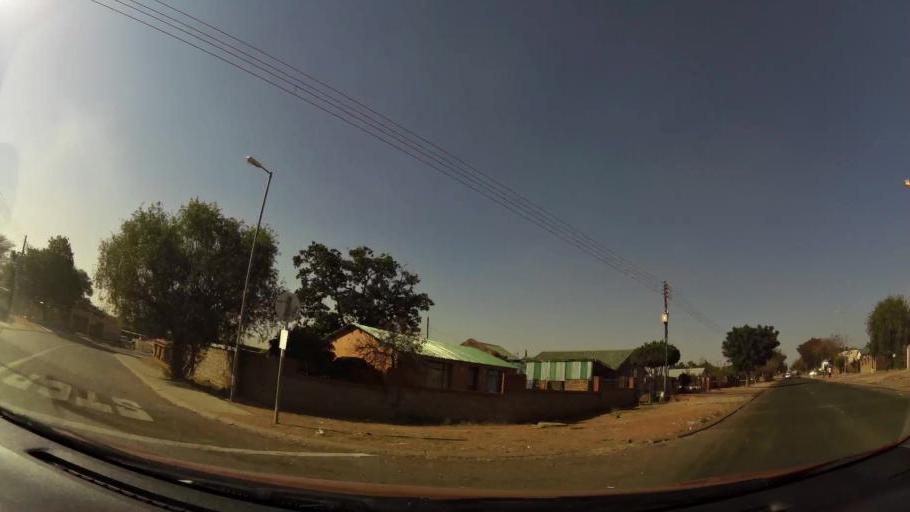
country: ZA
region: Gauteng
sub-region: City of Tshwane Metropolitan Municipality
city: Mabopane
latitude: -25.5238
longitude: 28.0965
